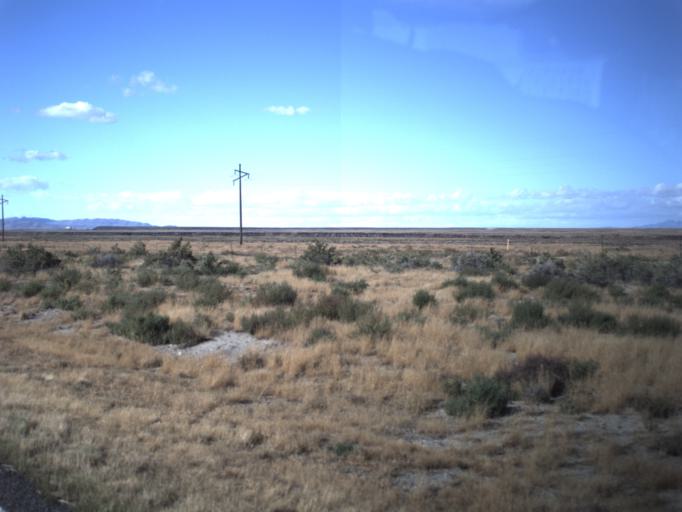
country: US
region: Utah
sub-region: Millard County
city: Delta
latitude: 39.2108
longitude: -112.6814
